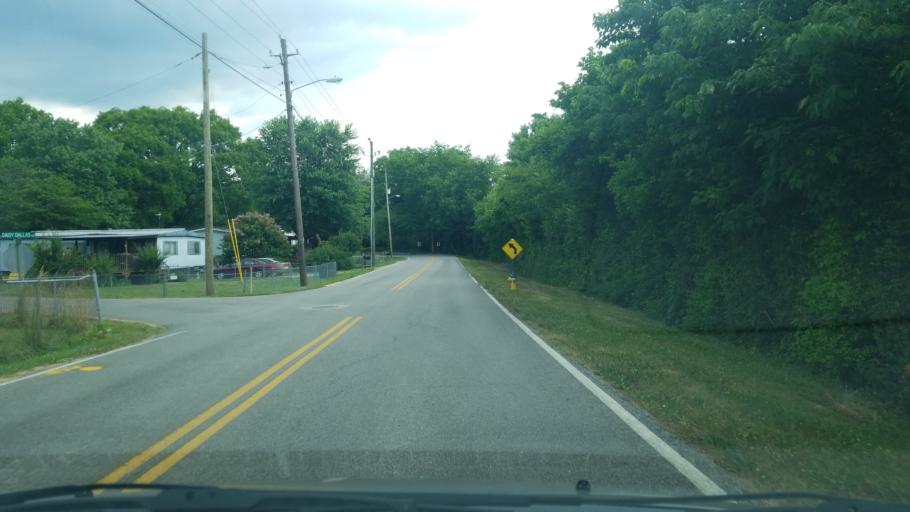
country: US
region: Tennessee
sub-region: Hamilton County
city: Soddy-Daisy
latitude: 35.2421
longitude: -85.1865
